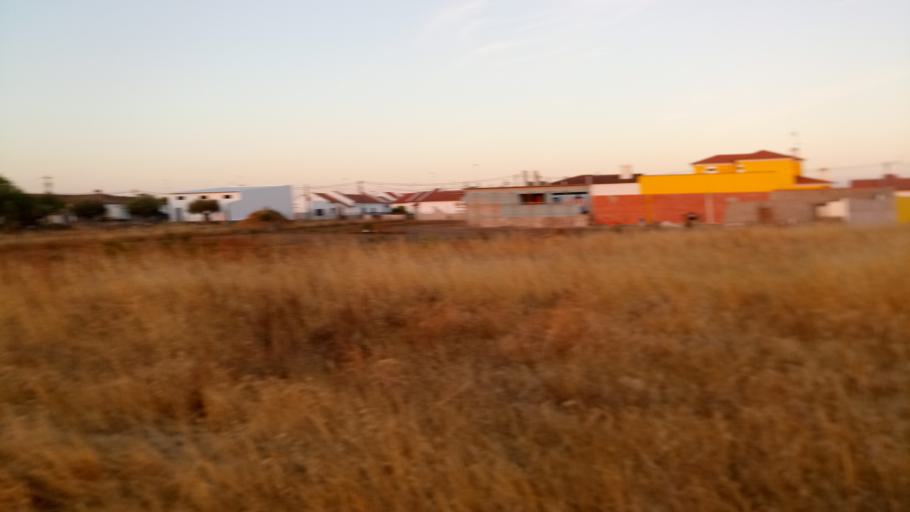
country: PT
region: Evora
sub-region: Reguengos de Monsaraz
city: Reguengos de Monsaraz
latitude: 38.3664
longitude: -7.4664
